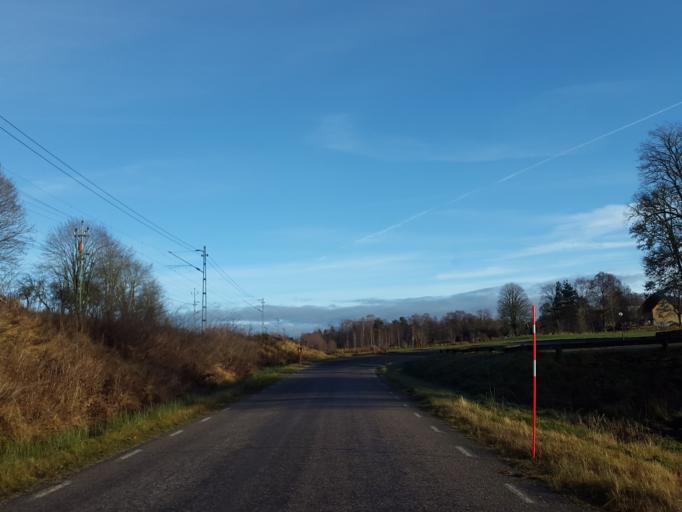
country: SE
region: Vaestra Goetaland
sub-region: Herrljunga Kommun
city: Herrljunga
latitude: 58.0635
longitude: 12.9506
